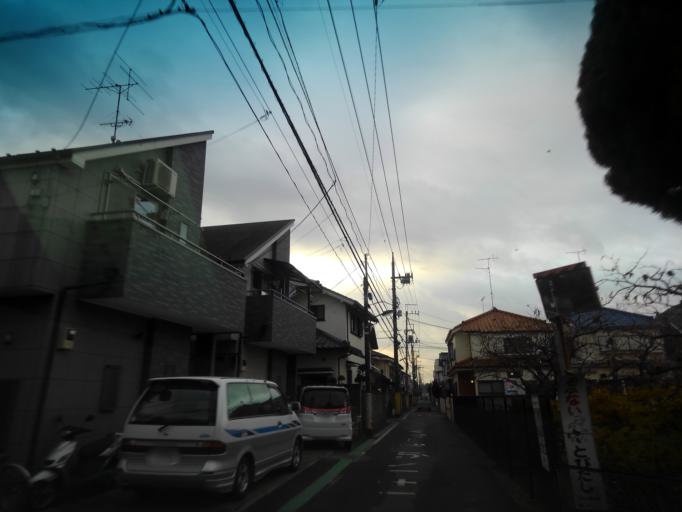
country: JP
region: Tokyo
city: Kokubunji
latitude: 35.7143
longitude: 139.4493
